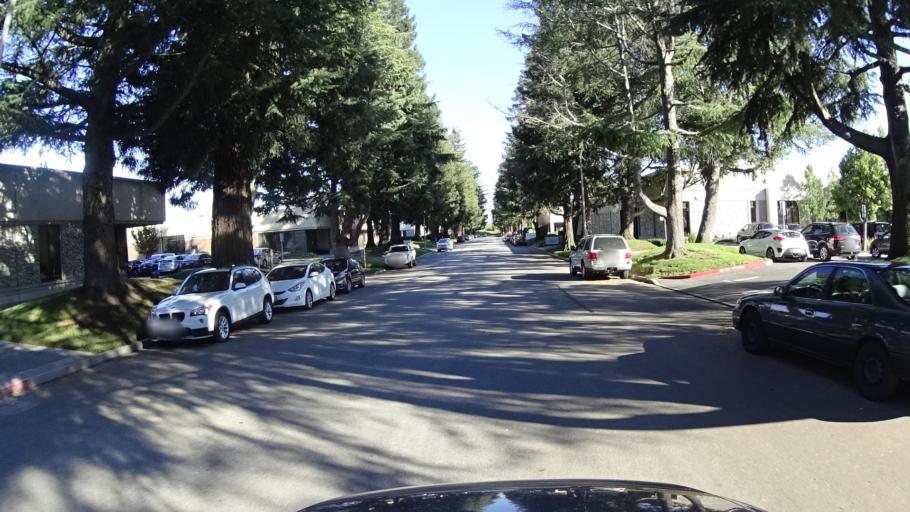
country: US
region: California
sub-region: Santa Clara County
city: Sunnyvale
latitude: 37.3715
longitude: -122.0011
